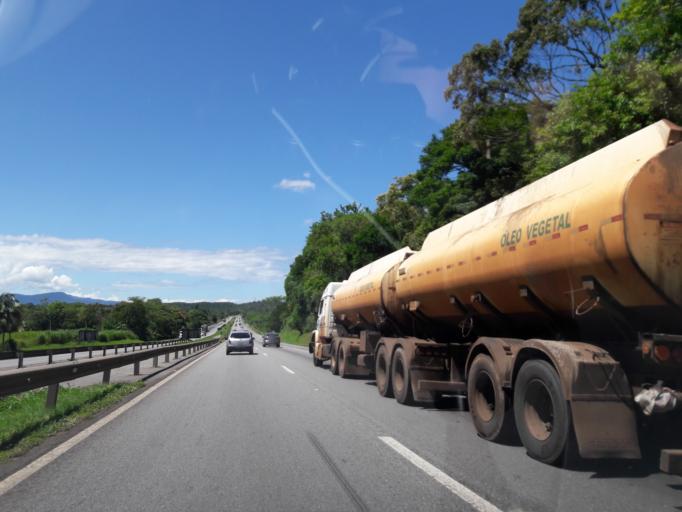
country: BR
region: Parana
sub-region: Antonina
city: Antonina
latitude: -25.5351
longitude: -48.7612
